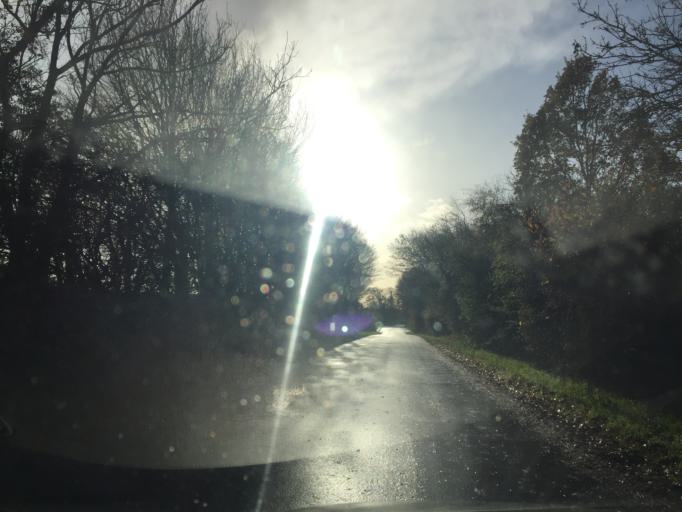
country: DK
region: South Denmark
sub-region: Kolding Kommune
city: Sonder Bjert
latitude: 55.4632
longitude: 9.6196
